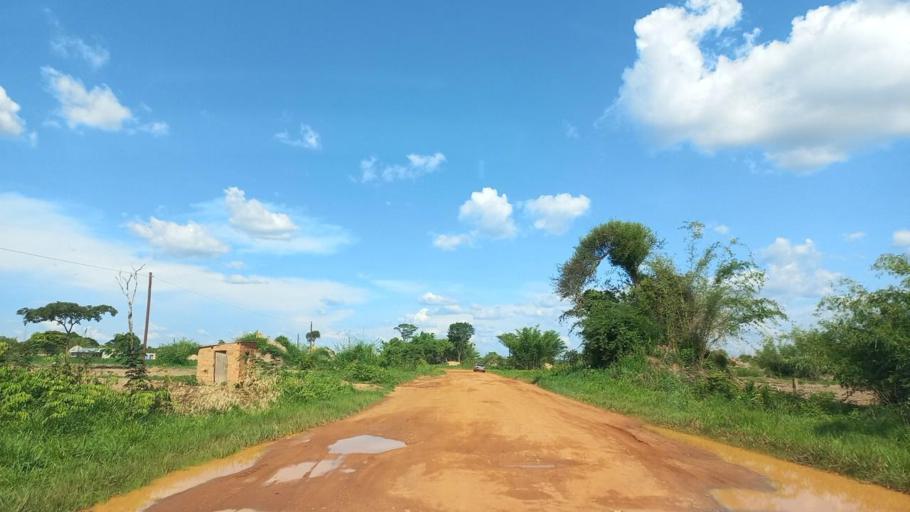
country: ZM
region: Copperbelt
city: Kitwe
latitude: -12.8637
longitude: 28.3791
